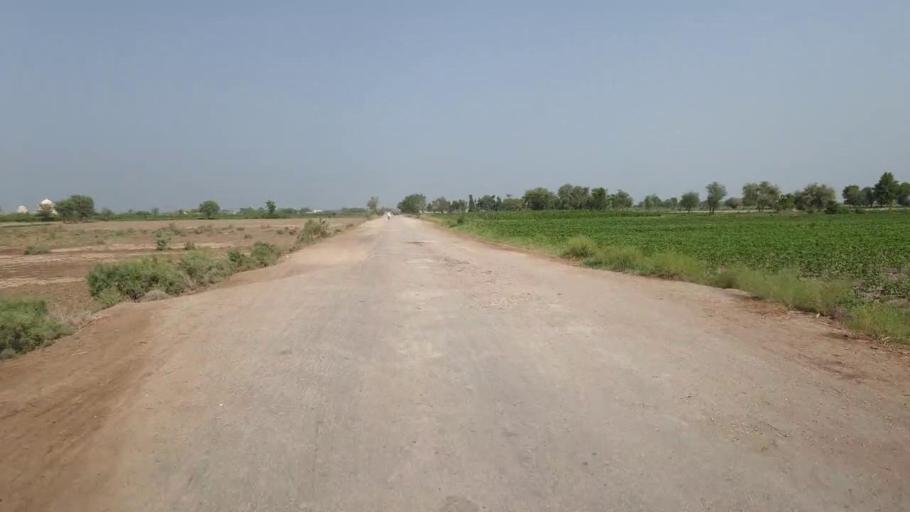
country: PK
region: Sindh
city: Daulatpur
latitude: 26.5504
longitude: 68.0572
